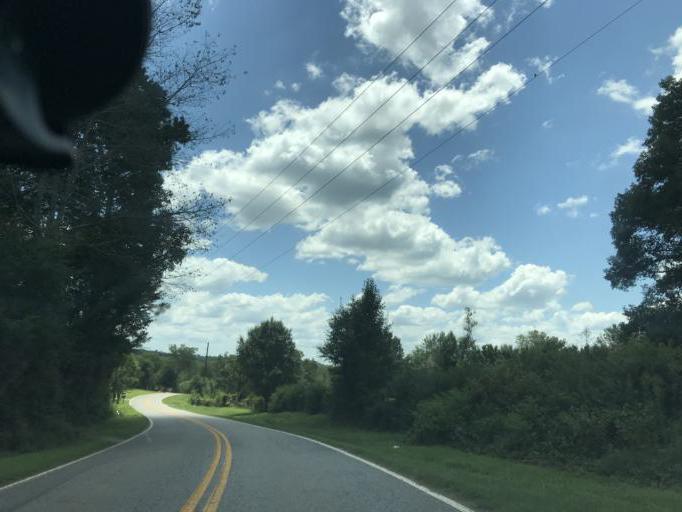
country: US
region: Georgia
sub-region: Fulton County
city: Milton
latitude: 34.2243
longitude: -84.2560
